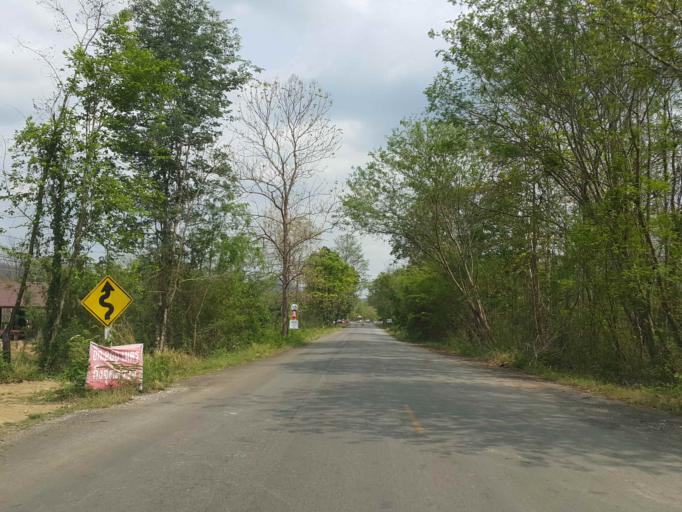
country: TH
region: Lampang
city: Thoen
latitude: 17.4597
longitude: 99.3663
